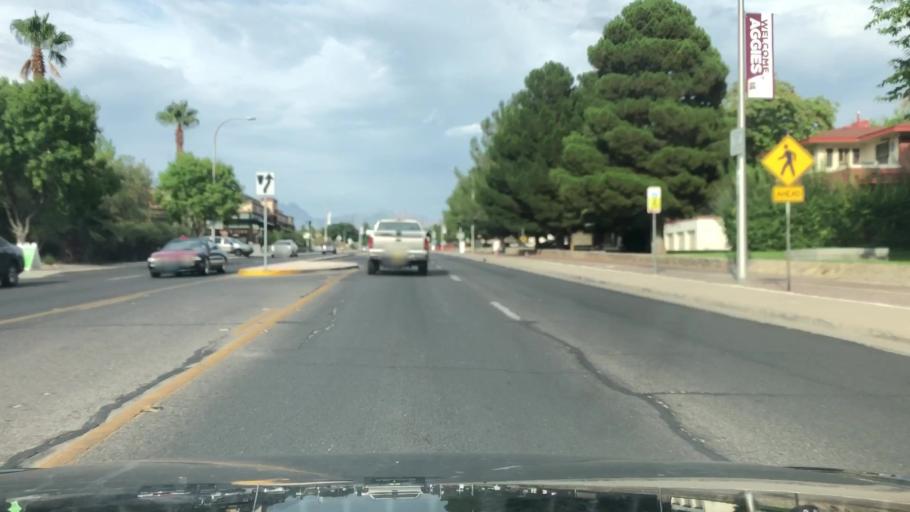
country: US
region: New Mexico
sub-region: Dona Ana County
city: University Park
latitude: 32.2842
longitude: -106.7555
